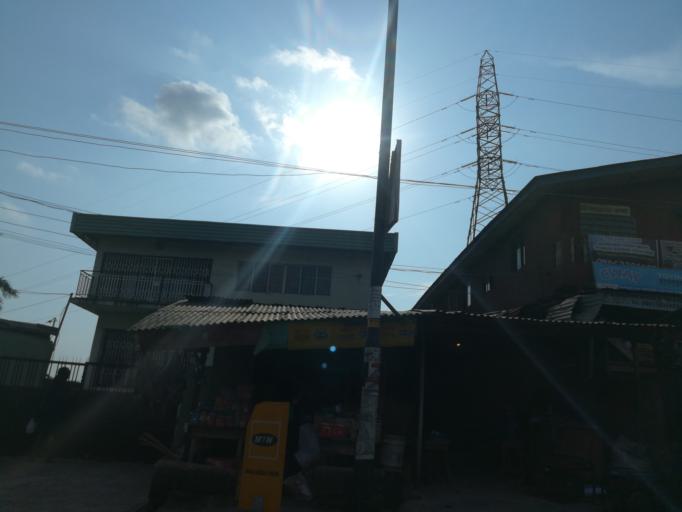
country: NG
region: Lagos
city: Ojota
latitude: 6.5927
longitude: 3.4004
